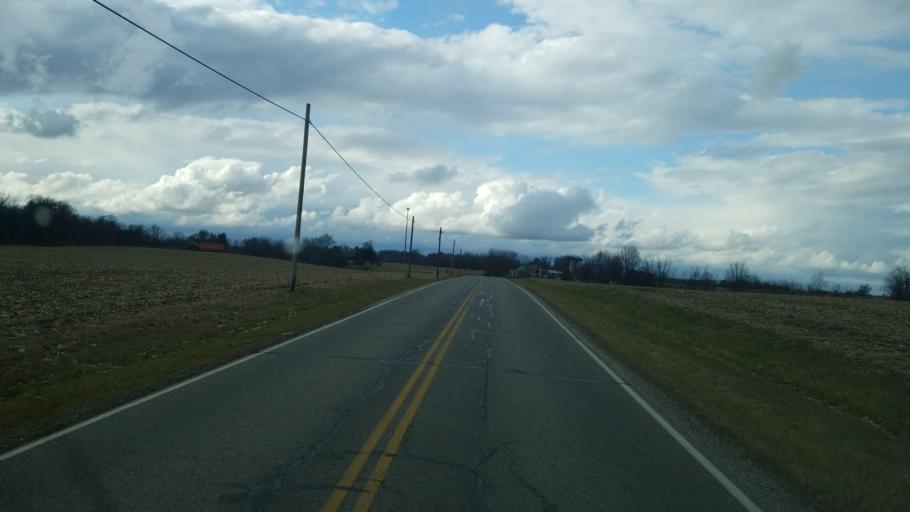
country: US
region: Ohio
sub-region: Crawford County
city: Bucyrus
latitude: 40.8069
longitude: -82.9991
